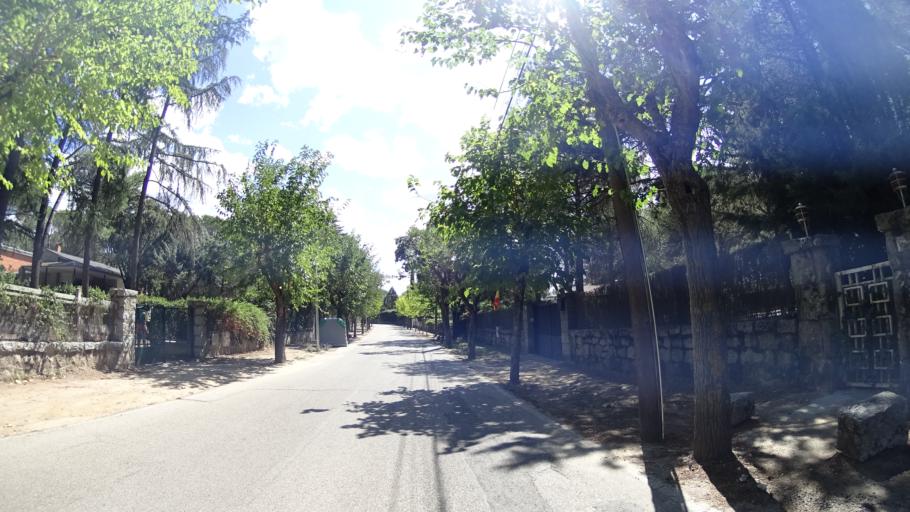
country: ES
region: Madrid
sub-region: Provincia de Madrid
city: Torrelodones
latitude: 40.5701
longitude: -3.9517
